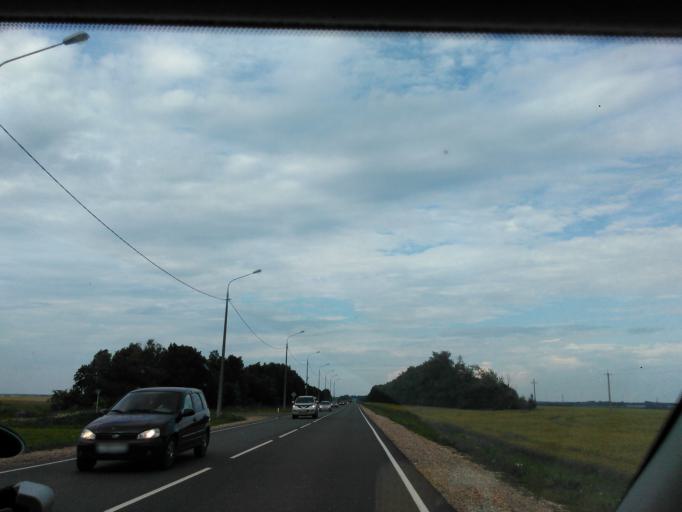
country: RU
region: Penza
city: Lermontovo
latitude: 52.9779
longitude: 43.6093
